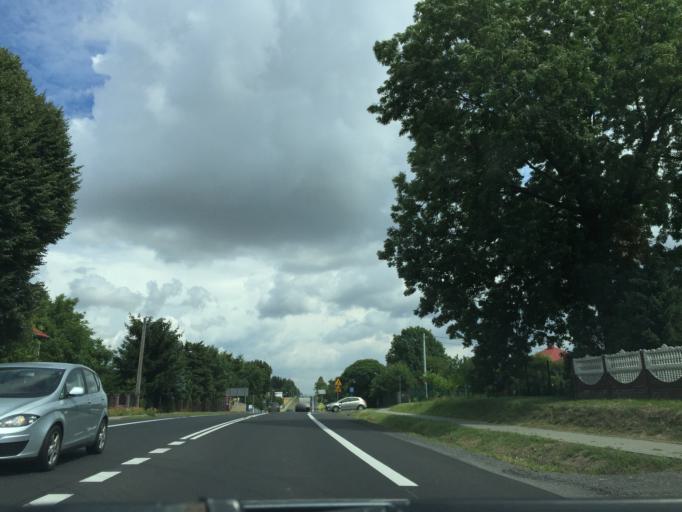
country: PL
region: Lesser Poland Voivodeship
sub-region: Powiat krakowski
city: Michalowice
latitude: 50.2035
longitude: 20.0128
